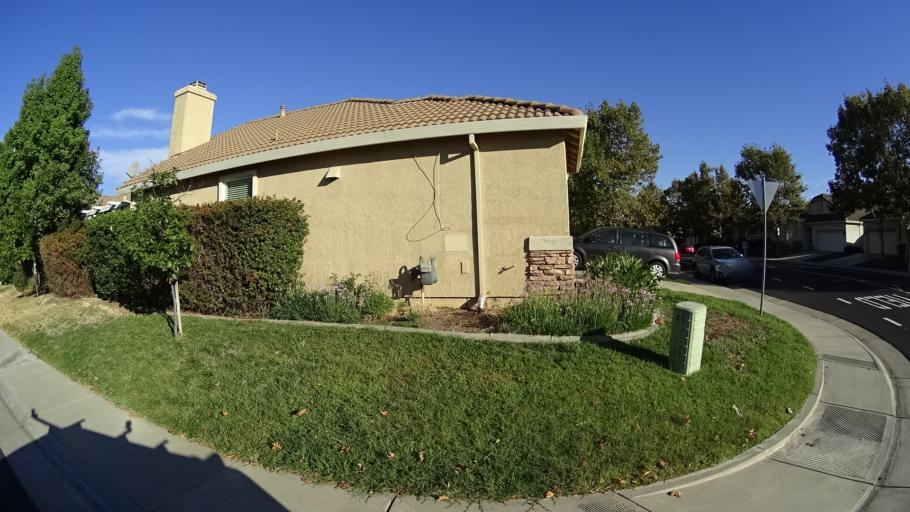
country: US
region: California
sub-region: Sacramento County
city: Laguna
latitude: 38.4022
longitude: -121.4796
